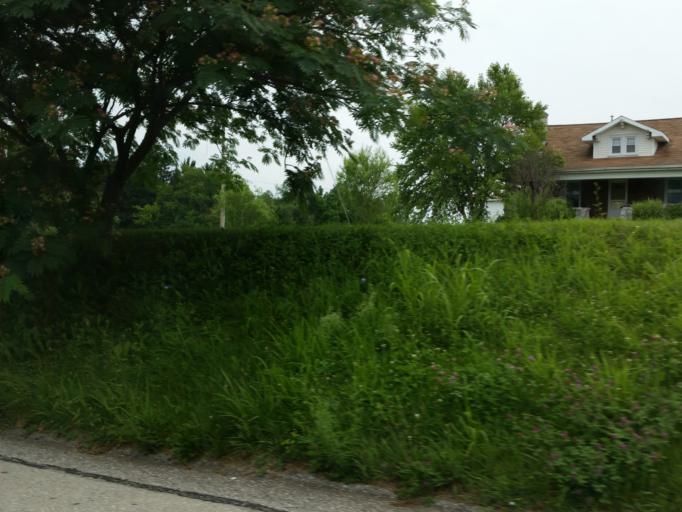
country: US
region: Pennsylvania
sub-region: York County
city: Emigsville
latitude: 40.0274
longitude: -76.7488
